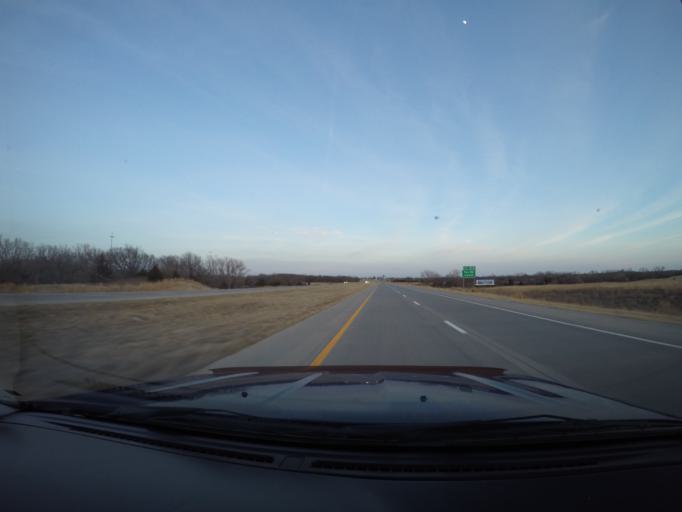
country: US
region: Kansas
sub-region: Dickinson County
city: Abilene
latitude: 38.9294
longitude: -97.2865
